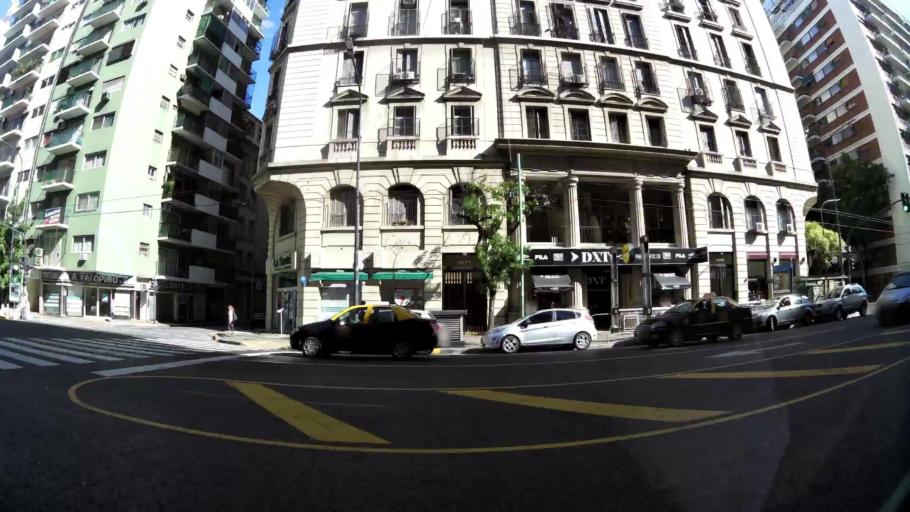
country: AR
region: Buenos Aires F.D.
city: Villa Santa Rita
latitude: -34.6234
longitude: -58.4483
